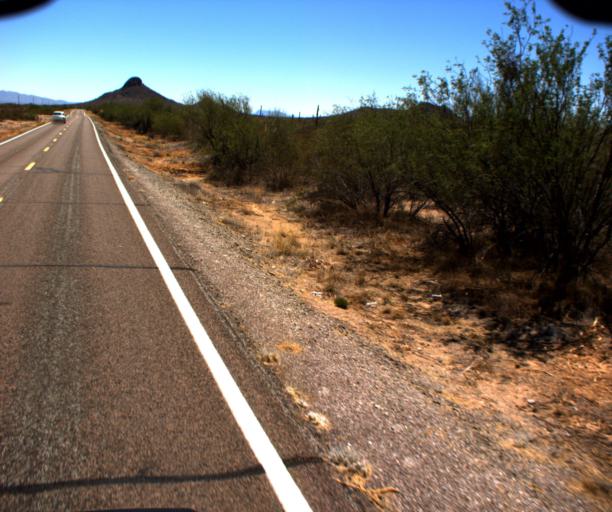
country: US
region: Arizona
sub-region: Pima County
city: Ajo
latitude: 32.2050
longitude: -112.5554
